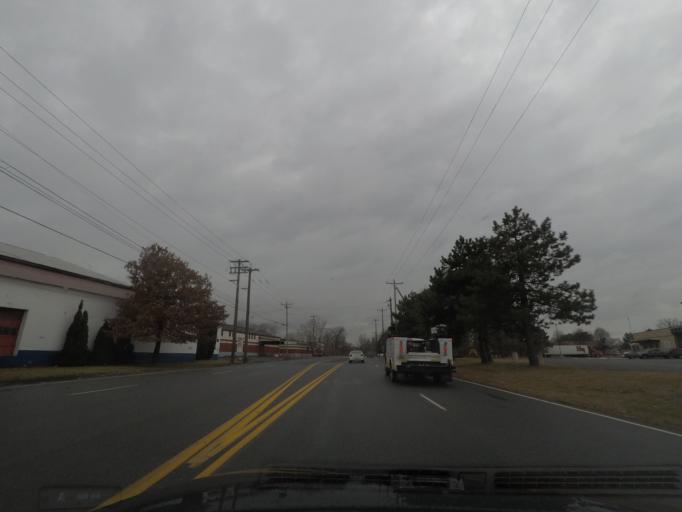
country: US
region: New York
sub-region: Albany County
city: Roessleville
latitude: 42.6978
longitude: -73.8263
